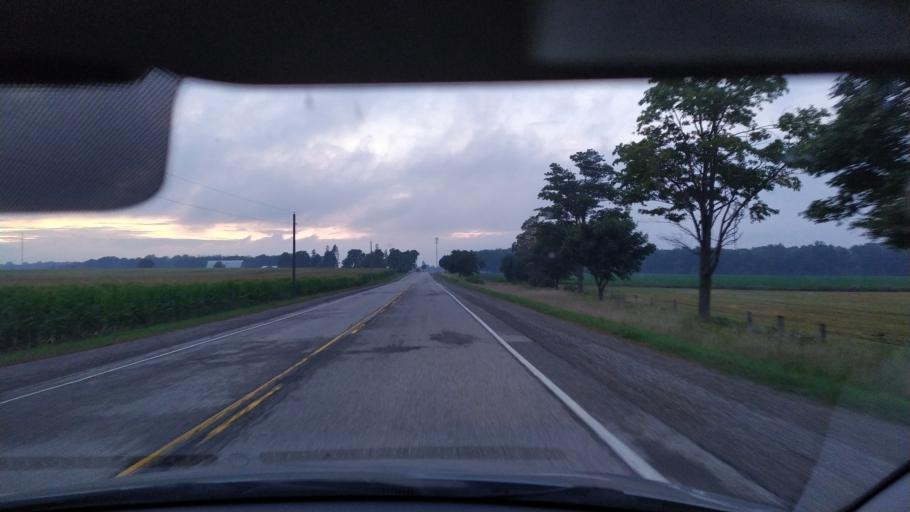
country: CA
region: Ontario
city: Kitchener
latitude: 43.3547
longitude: -80.7001
